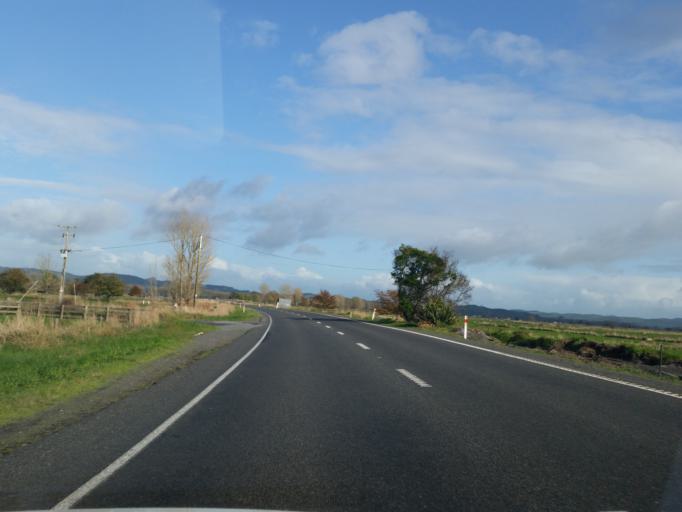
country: NZ
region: Waikato
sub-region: Hauraki District
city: Ngatea
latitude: -37.2763
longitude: 175.4640
